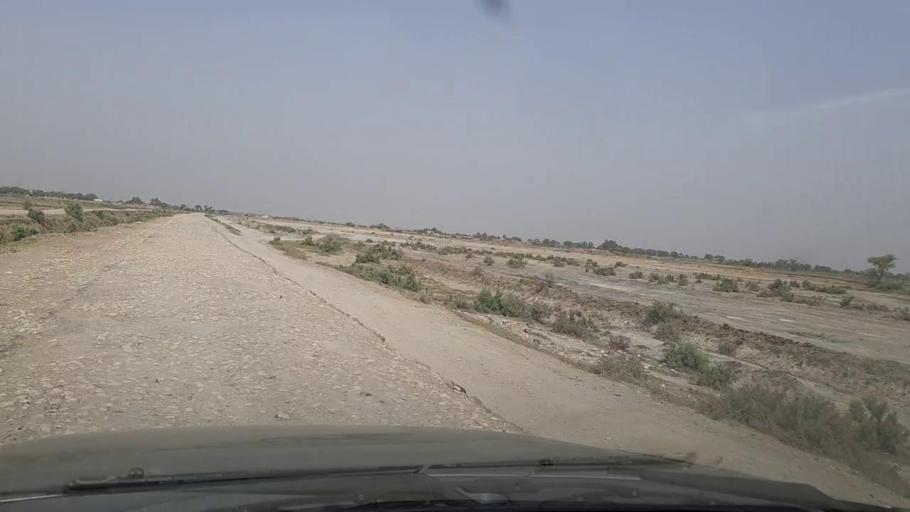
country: PK
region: Balochistan
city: Sohbatpur
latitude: 28.4120
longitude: 68.6952
